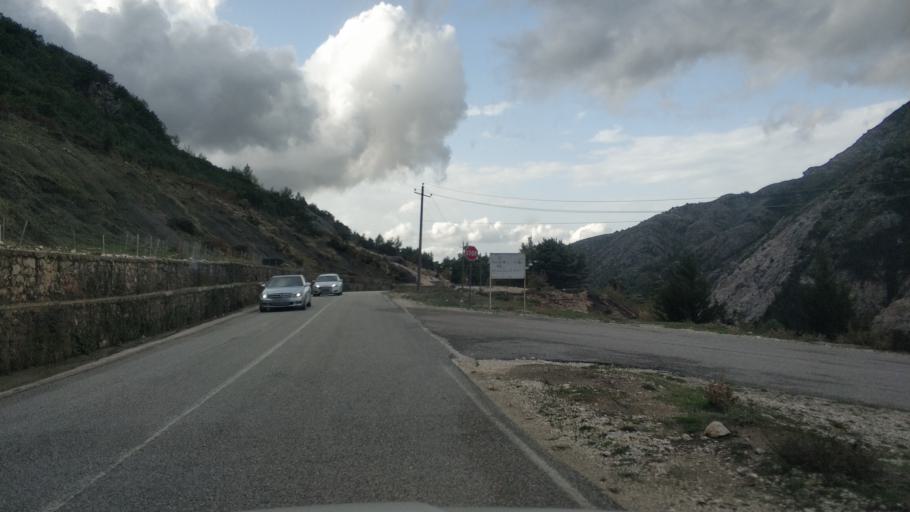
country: AL
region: Vlore
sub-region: Rrethi i Vlores
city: Orikum
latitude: 40.2470
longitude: 19.5464
